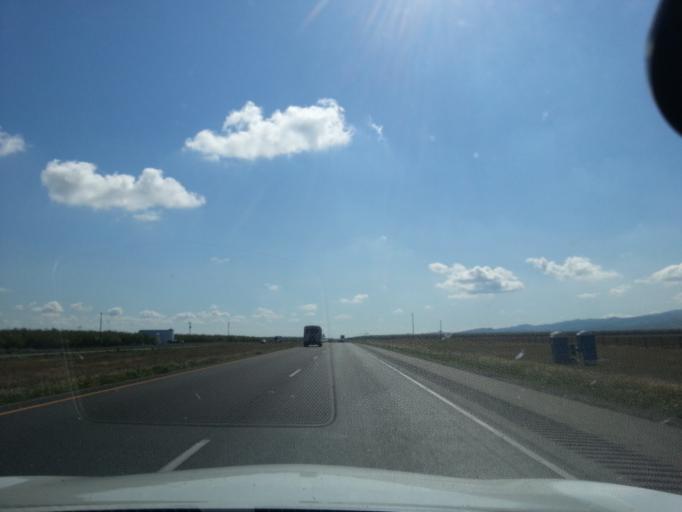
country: US
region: California
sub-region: Fresno County
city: San Joaquin
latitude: 36.4236
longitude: -120.3836
